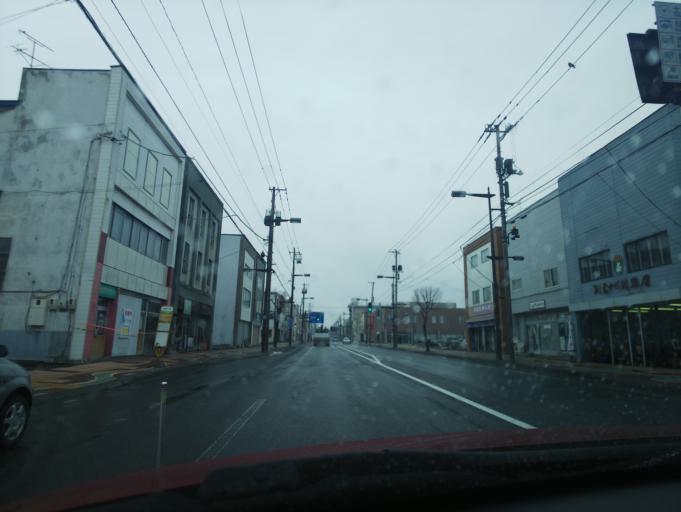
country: JP
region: Hokkaido
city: Nayoro
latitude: 44.1743
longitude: 142.3929
